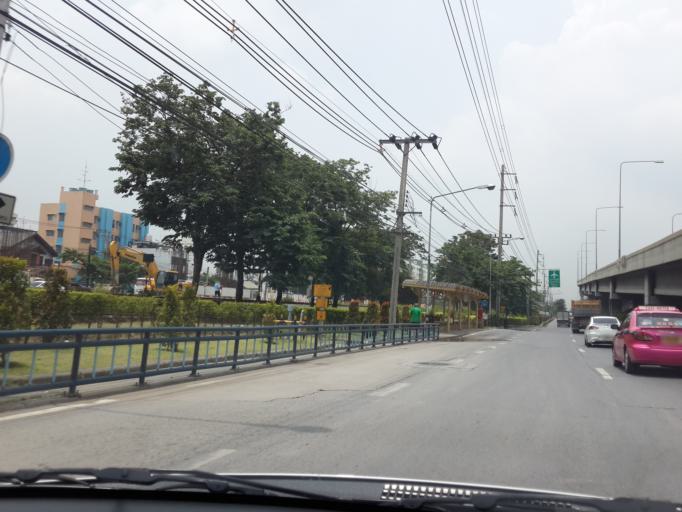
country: TH
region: Bangkok
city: Lak Si
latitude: 13.8885
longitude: 100.5836
